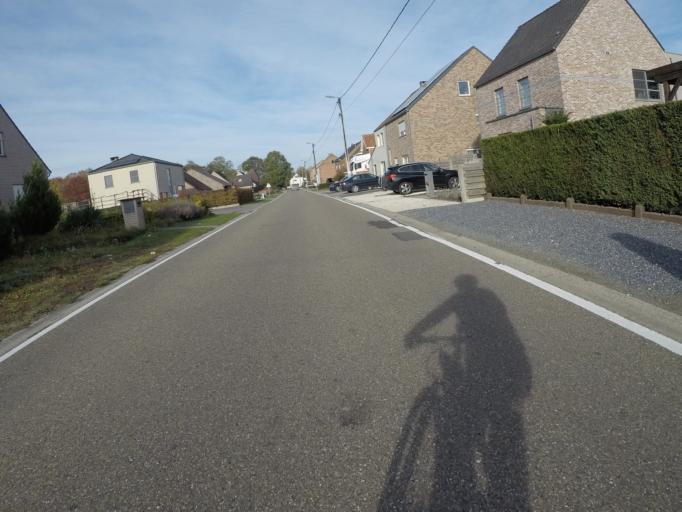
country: BE
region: Flanders
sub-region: Provincie Vlaams-Brabant
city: Begijnendijk
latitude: 51.0170
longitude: 4.7971
